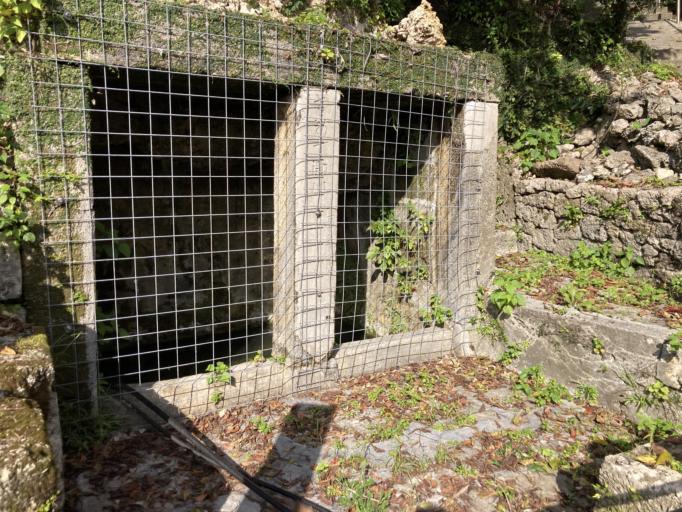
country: JP
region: Okinawa
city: Tomigusuku
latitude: 26.1854
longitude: 127.7567
